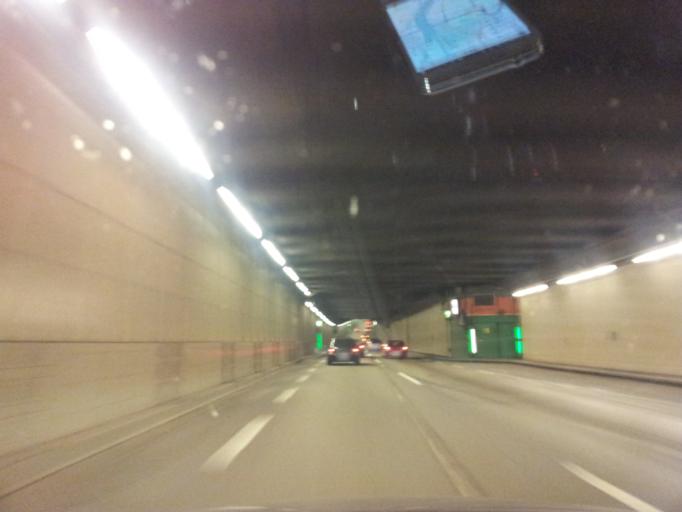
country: CH
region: Basel-City
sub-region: Basel-Stadt
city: Basel
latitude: 47.5708
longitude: 7.5891
